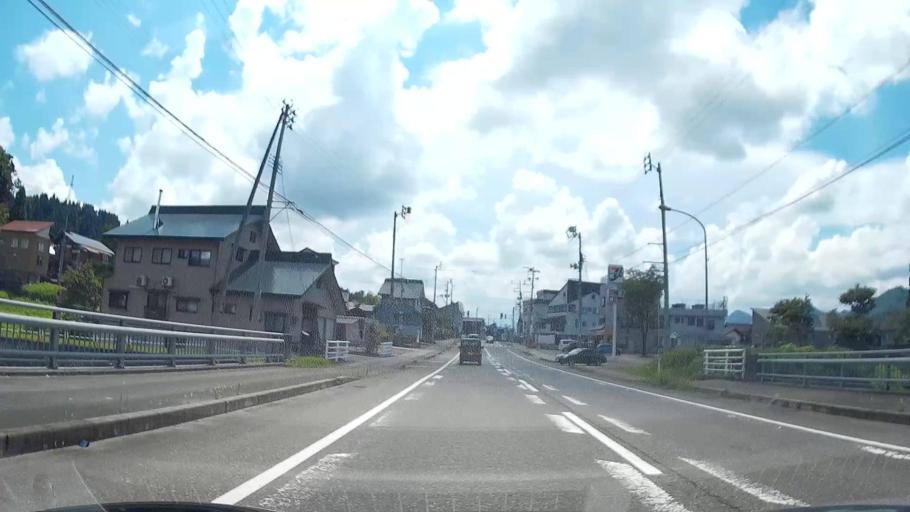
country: JP
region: Niigata
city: Tokamachi
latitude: 37.0553
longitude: 138.7006
